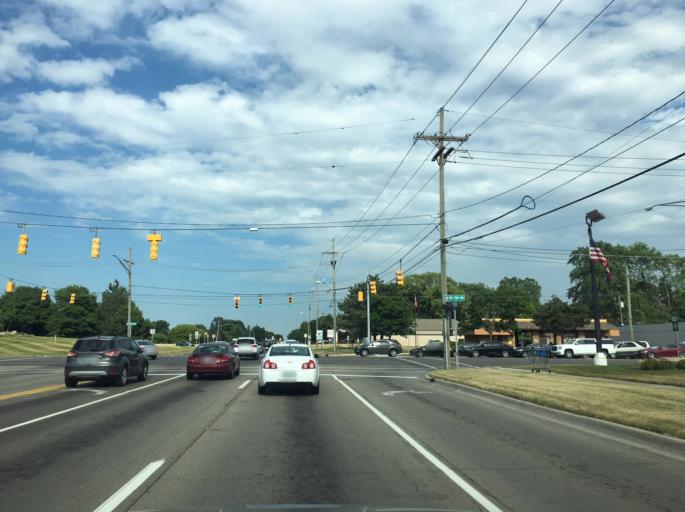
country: US
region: Michigan
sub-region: Macomb County
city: Sterling Heights
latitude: 42.5366
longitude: -83.0299
